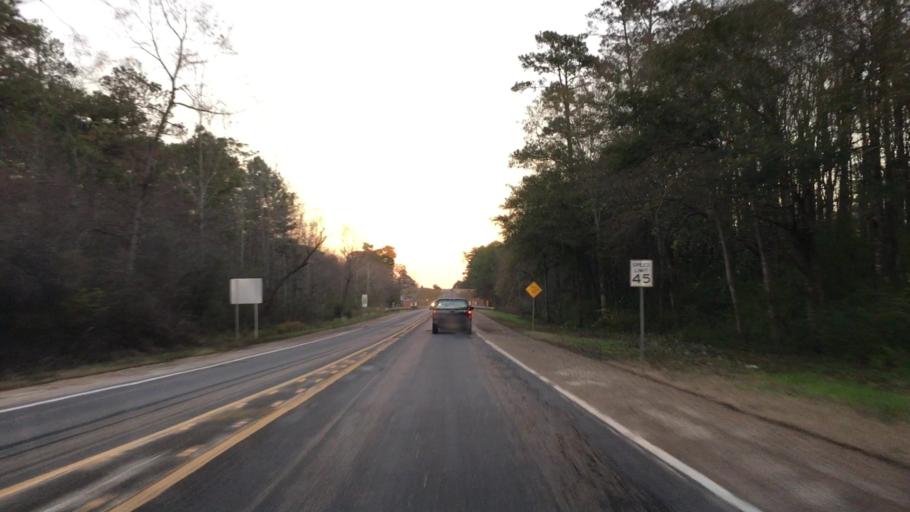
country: US
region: Louisiana
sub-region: Vernon Parish
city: Fort Polk South
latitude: 31.0299
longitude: -93.2158
